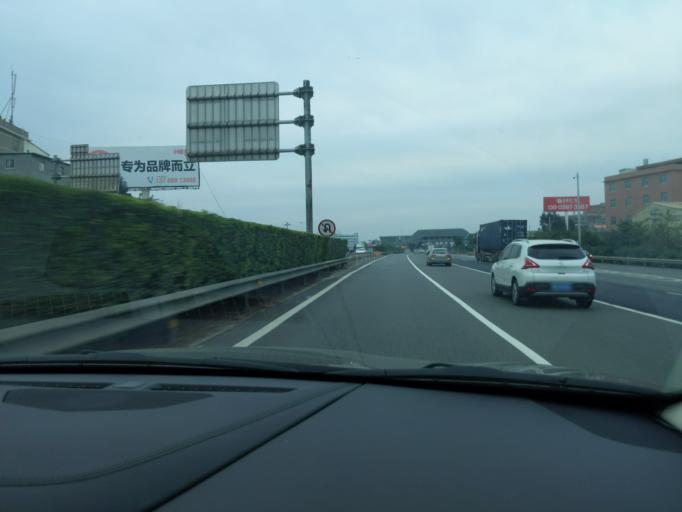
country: CN
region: Fujian
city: Anhai
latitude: 24.7450
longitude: 118.4289
